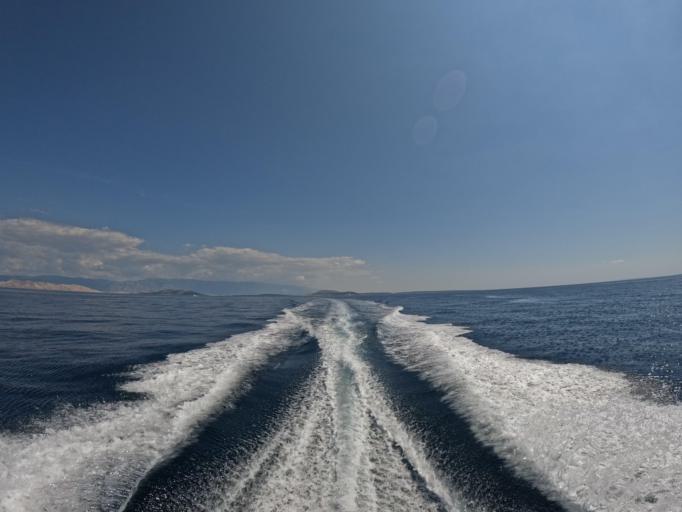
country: HR
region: Primorsko-Goranska
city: Punat
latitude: 44.9002
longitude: 14.6138
